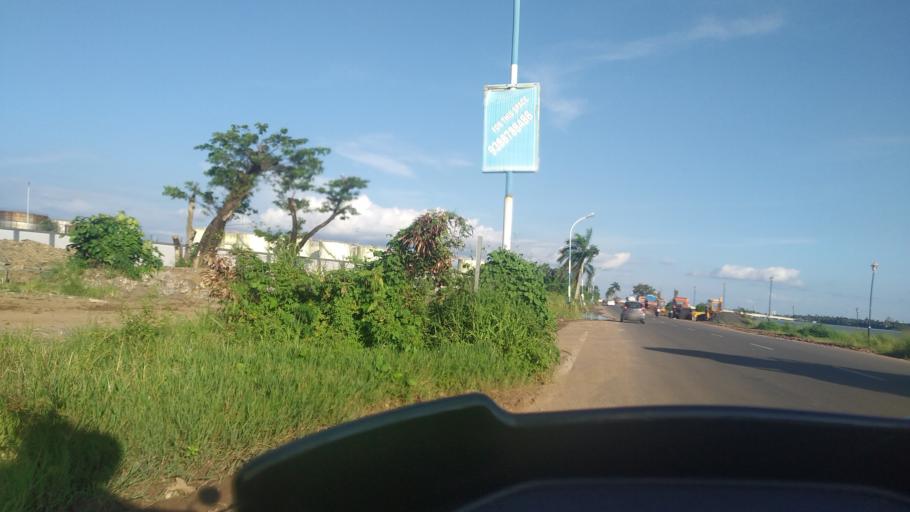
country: IN
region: Kerala
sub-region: Ernakulam
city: Cochin
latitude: 9.9334
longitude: 76.2748
